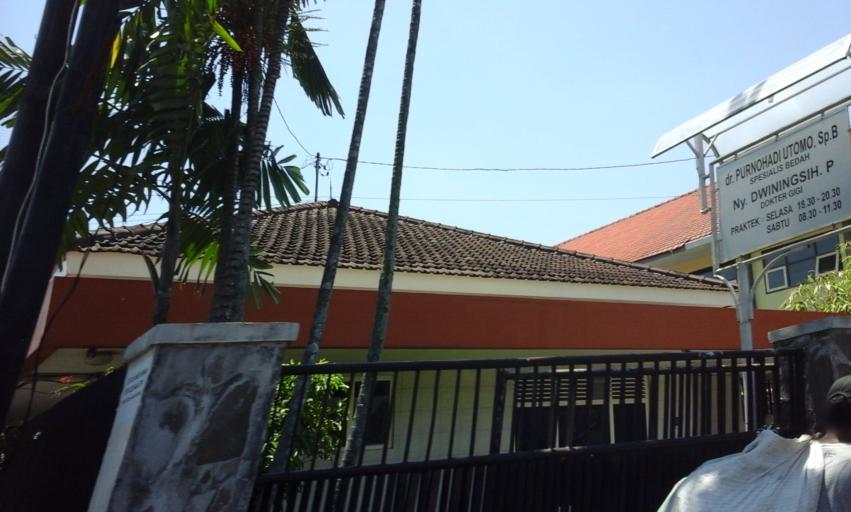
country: ID
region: East Java
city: Jember
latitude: -8.1665
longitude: 113.7045
